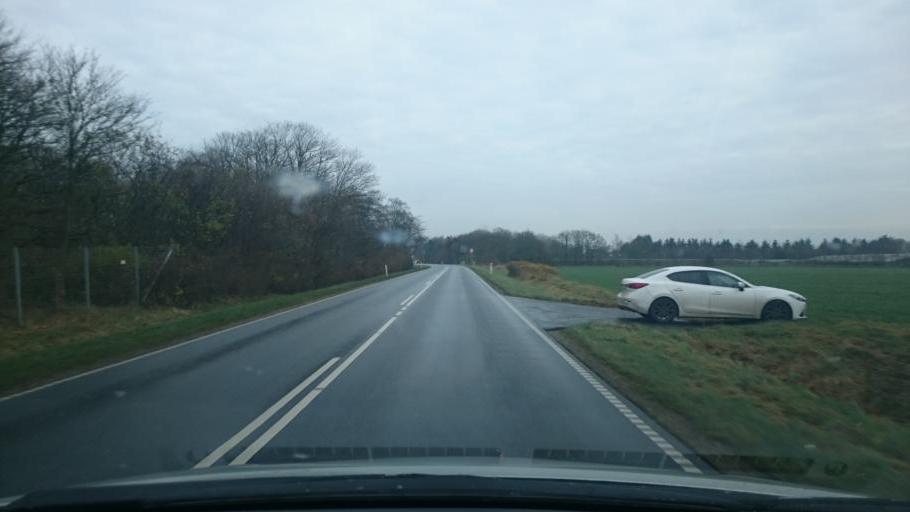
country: DK
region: South Denmark
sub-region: Esbjerg Kommune
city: Ribe
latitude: 55.3322
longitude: 8.8699
